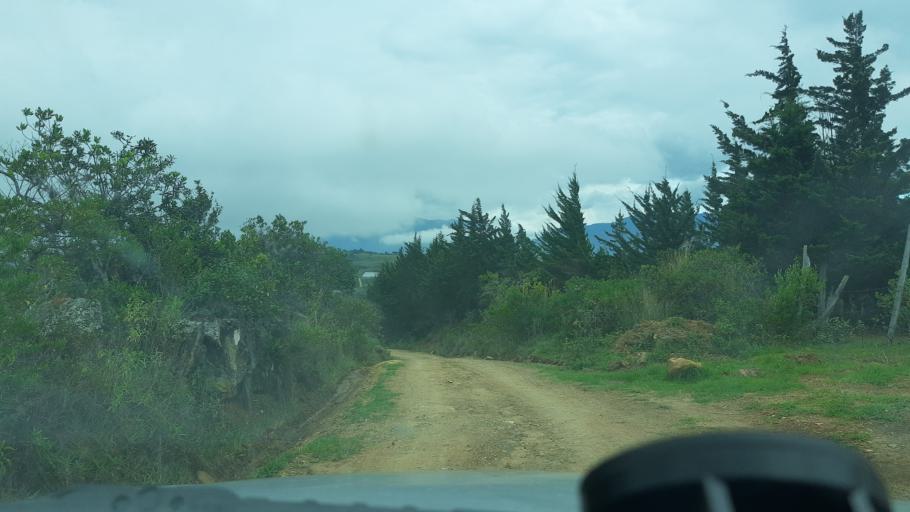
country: CO
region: Boyaca
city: Santa Sofia
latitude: 5.7134
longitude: -73.5937
